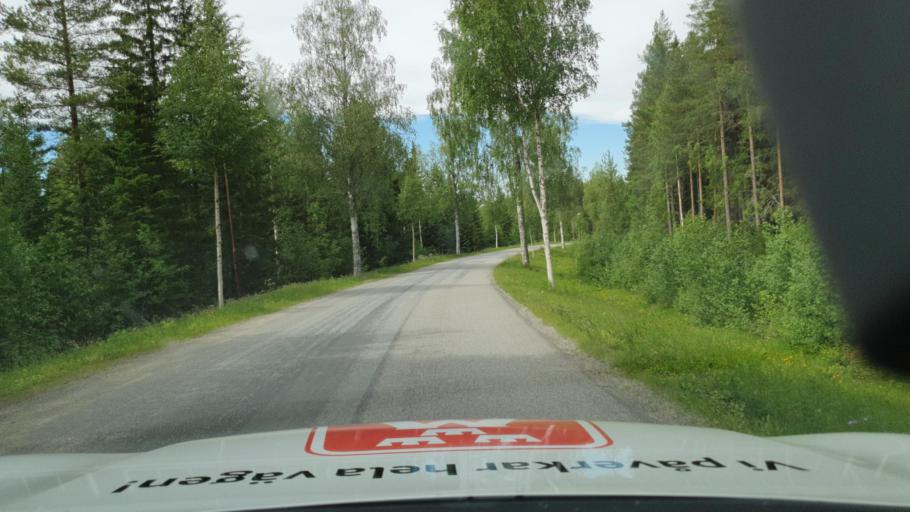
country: SE
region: Vaesterbotten
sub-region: Skelleftea Kommun
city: Burtraesk
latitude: 64.4424
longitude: 20.4872
